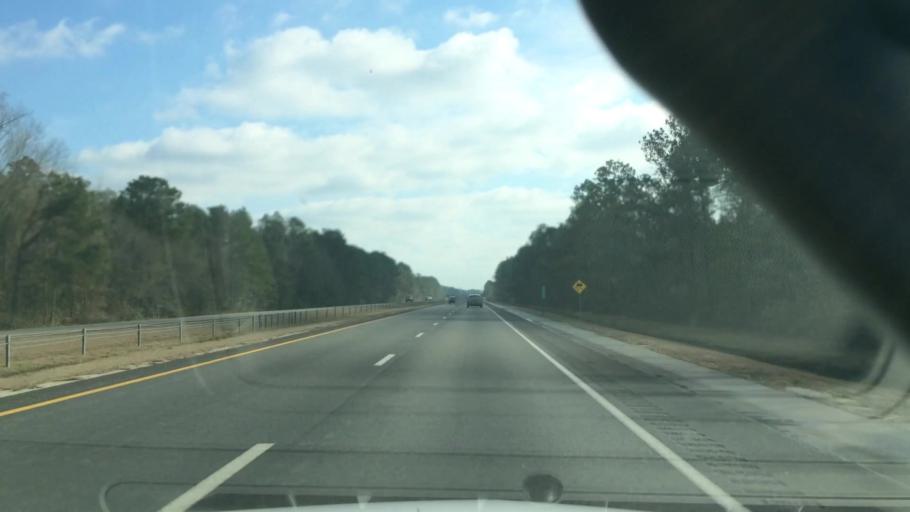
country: US
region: North Carolina
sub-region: Pender County
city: Burgaw
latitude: 34.6201
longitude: -77.9289
